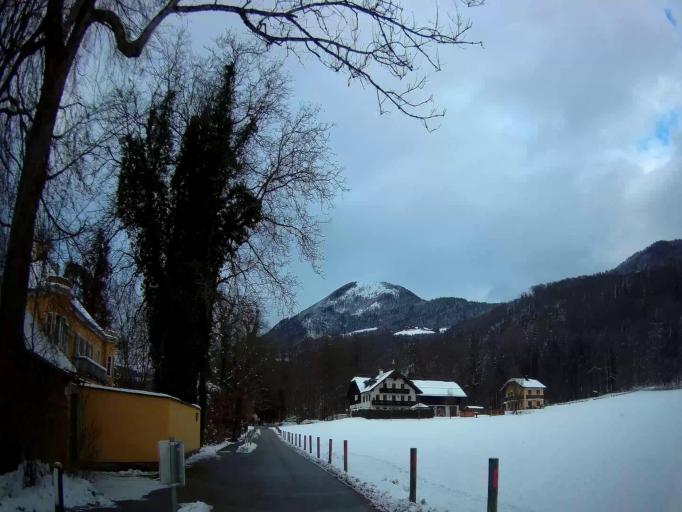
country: AT
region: Salzburg
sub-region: Politischer Bezirk Salzburg-Umgebung
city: Elsbethen
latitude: 47.7814
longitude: 13.0897
